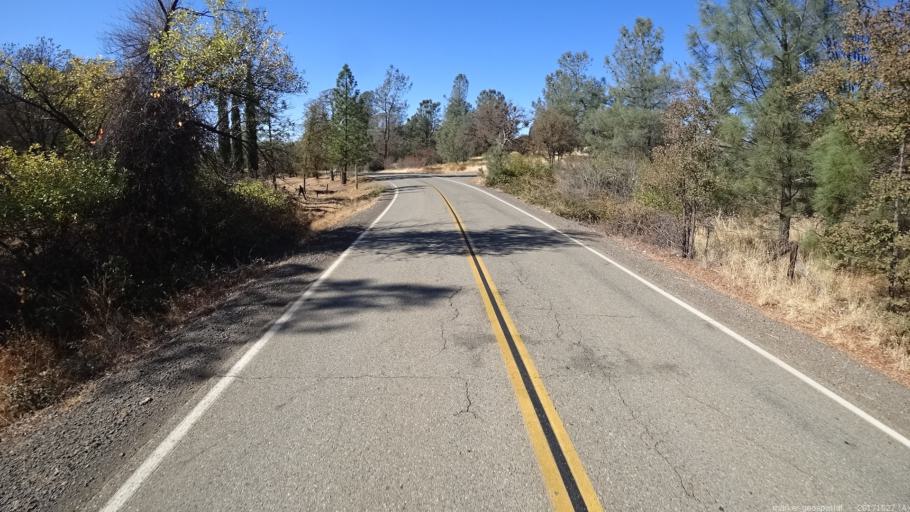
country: US
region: California
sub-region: Shasta County
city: Bella Vista
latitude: 40.6851
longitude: -122.0376
